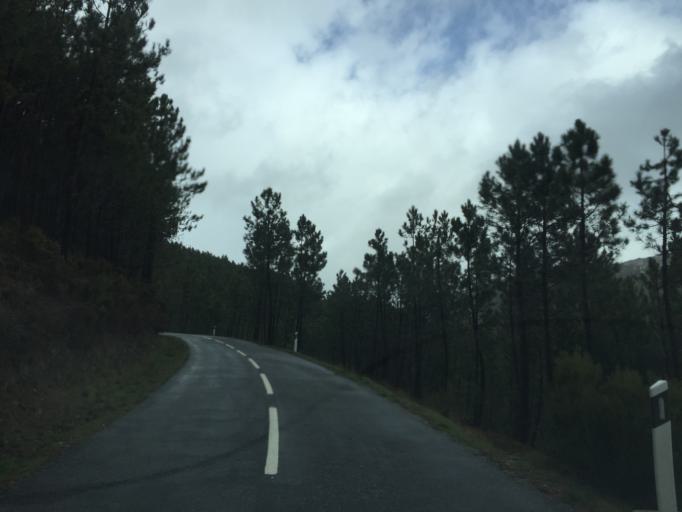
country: PT
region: Guarda
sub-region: Seia
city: Seia
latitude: 40.3319
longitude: -7.7164
